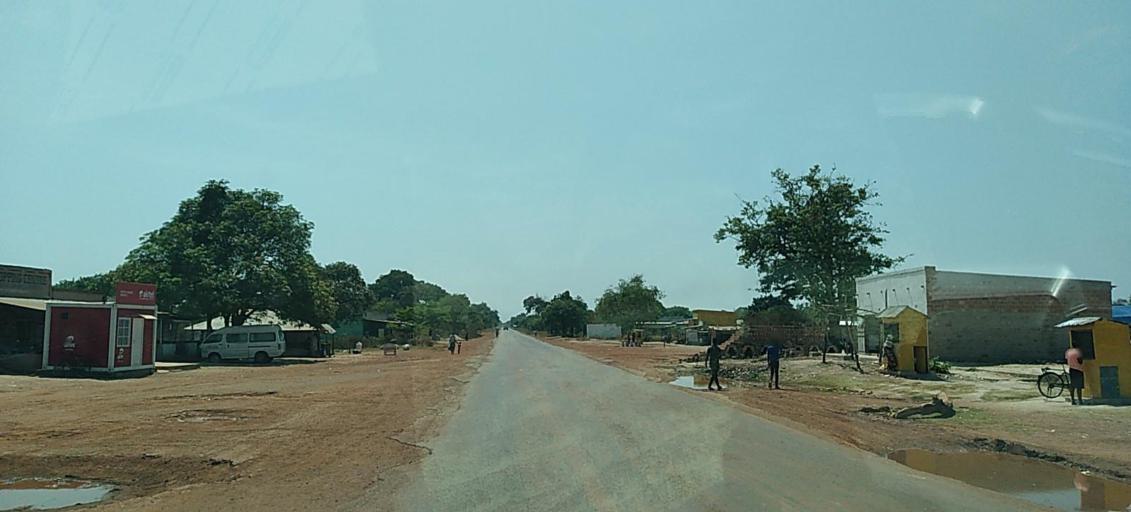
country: ZM
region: North-Western
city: Solwezi
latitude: -12.3614
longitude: 25.9409
